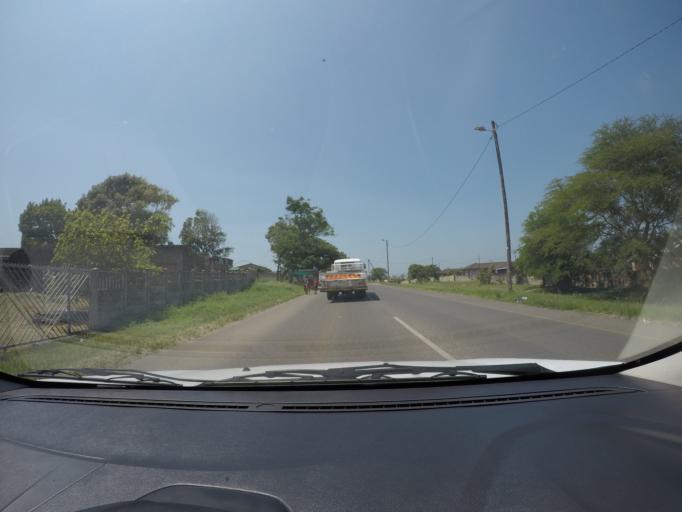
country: ZA
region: KwaZulu-Natal
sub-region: uThungulu District Municipality
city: eSikhawini
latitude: -28.8659
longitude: 31.9260
